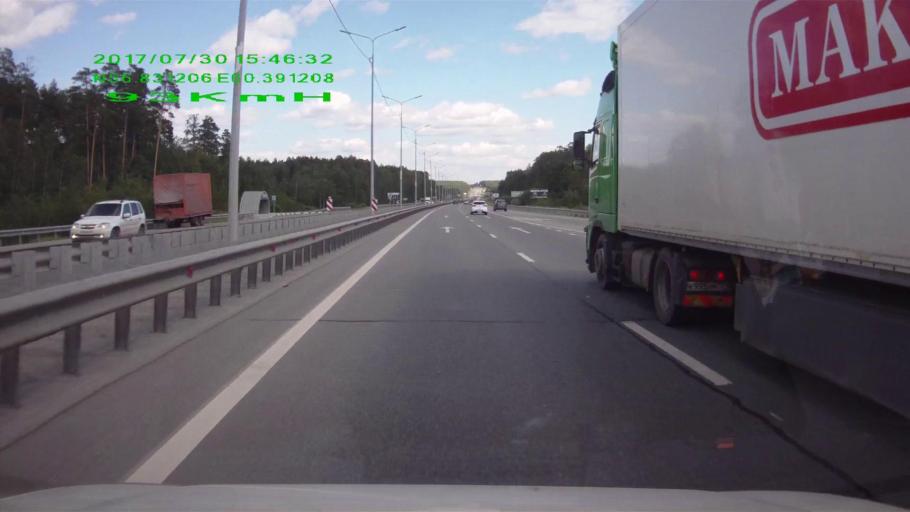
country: RU
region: Sverdlovsk
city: Severka
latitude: 56.8312
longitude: 60.3920
